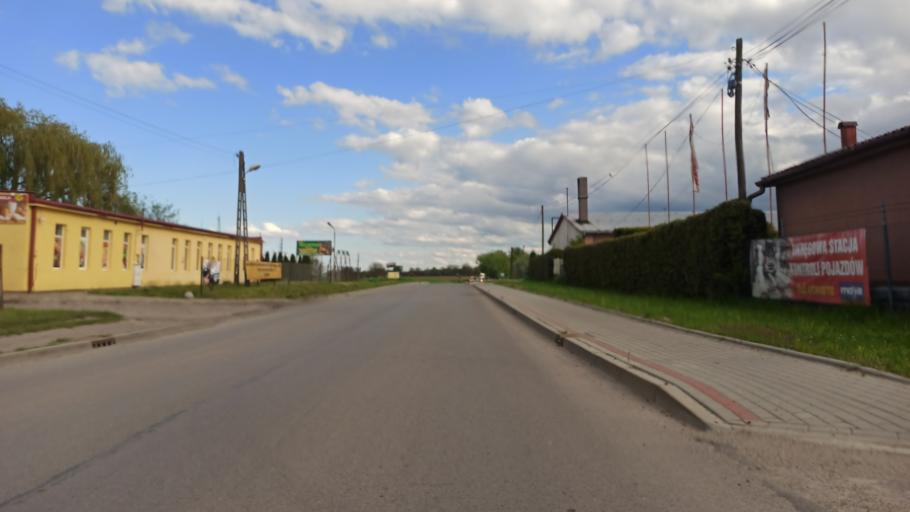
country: PL
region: Subcarpathian Voivodeship
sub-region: Powiat jaroslawski
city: Radymno
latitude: 49.9377
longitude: 22.8352
